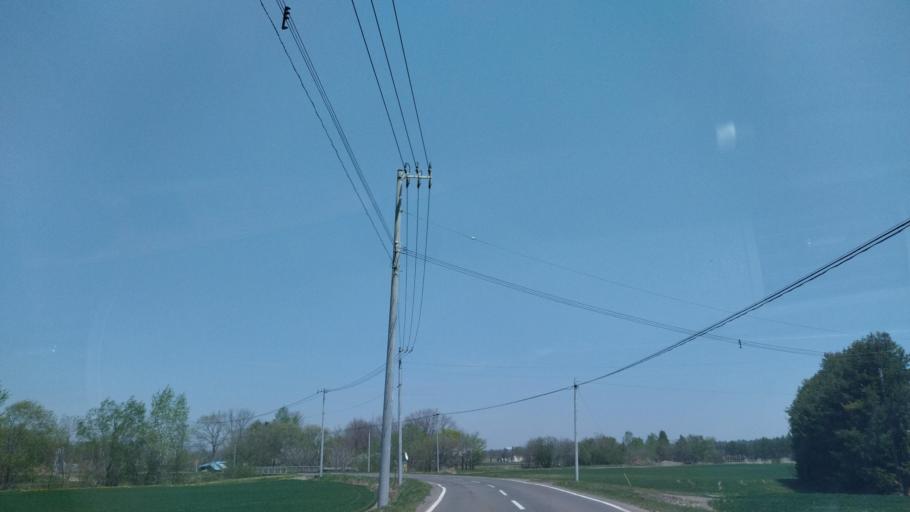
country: JP
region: Hokkaido
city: Obihiro
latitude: 42.8927
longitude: 143.0290
